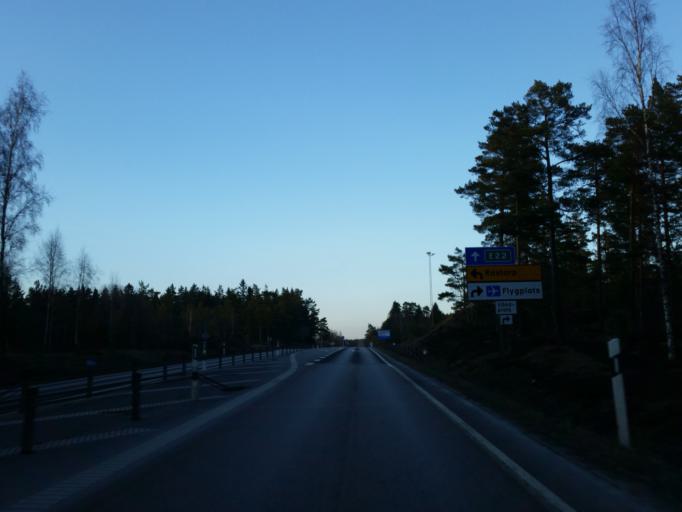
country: SE
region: Kalmar
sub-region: Oskarshamns Kommun
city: Oskarshamn
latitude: 57.3499
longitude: 16.4909
